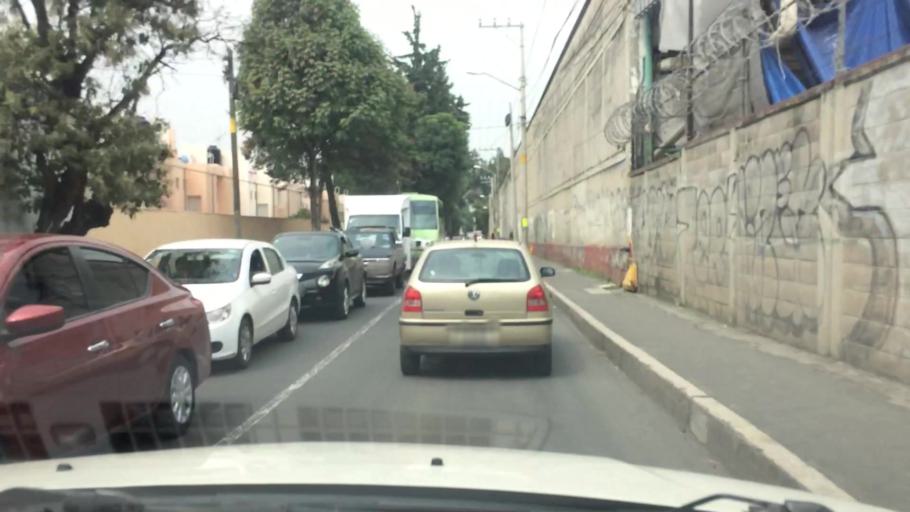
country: MX
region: Mexico City
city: Xochimilco
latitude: 19.2707
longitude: -99.1264
